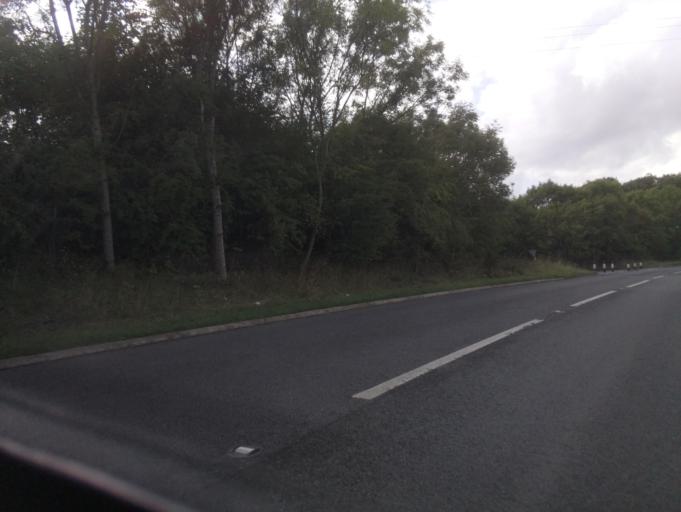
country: GB
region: England
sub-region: Darlington
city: High Coniscliffe
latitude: 54.4671
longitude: -1.6617
